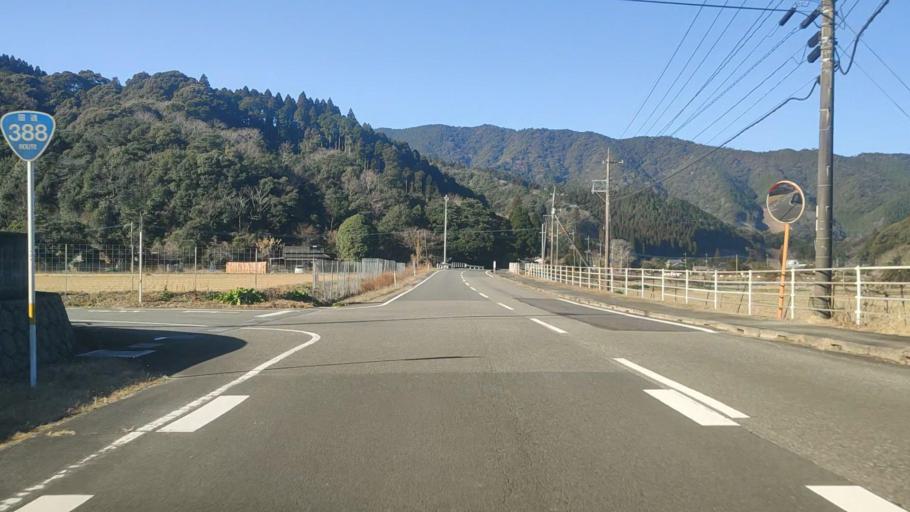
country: JP
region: Miyazaki
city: Nobeoka
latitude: 32.7465
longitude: 131.8133
